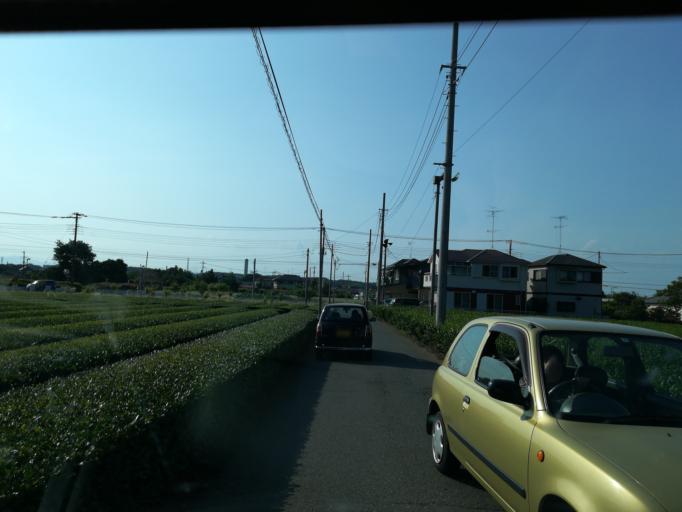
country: JP
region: Saitama
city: Sayama
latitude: 35.7995
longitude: 139.3925
